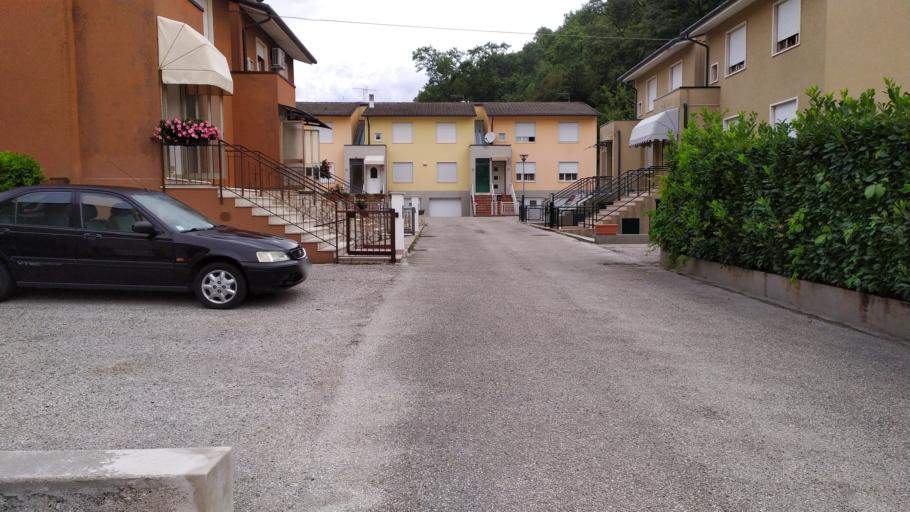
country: IT
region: Veneto
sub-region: Provincia di Vicenza
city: Malo
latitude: 45.6595
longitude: 11.3985
